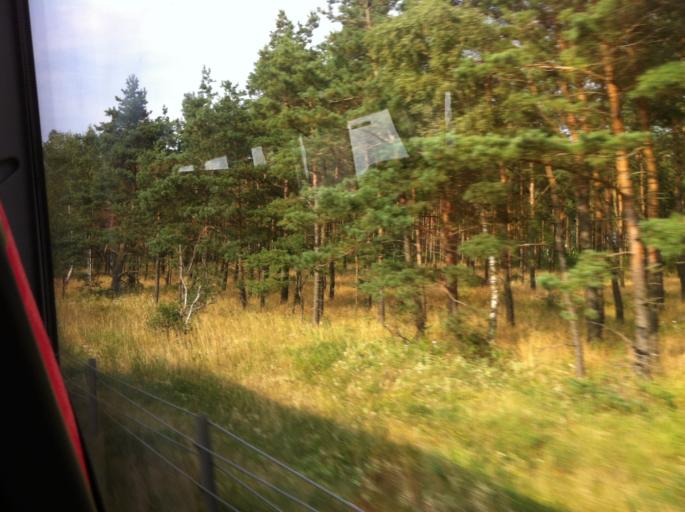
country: SE
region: Skane
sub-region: Kristianstads Kommun
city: Norra Asum
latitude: 55.9327
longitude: 14.0753
